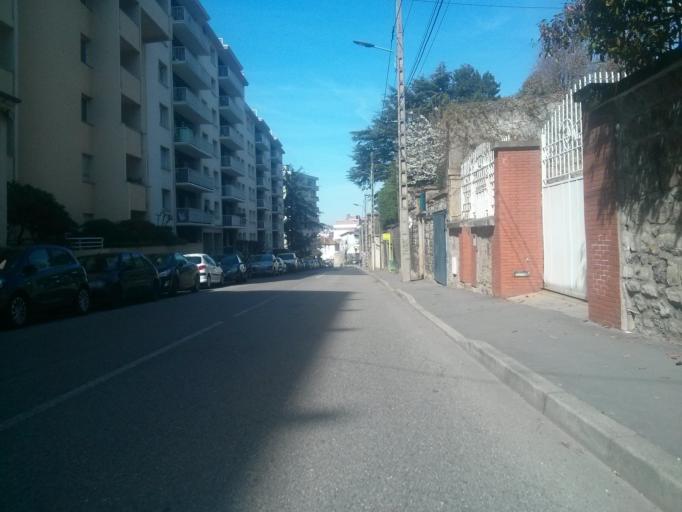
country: FR
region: Rhone-Alpes
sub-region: Departement de la Loire
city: Saint-Etienne
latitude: 45.4296
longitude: 4.3991
